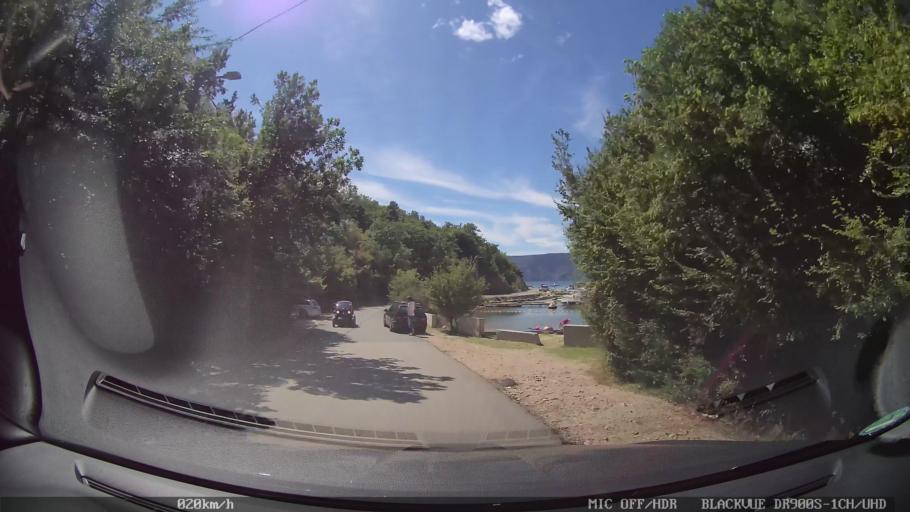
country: HR
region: Primorsko-Goranska
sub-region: Grad Krk
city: Krk
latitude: 45.0401
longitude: 14.4787
